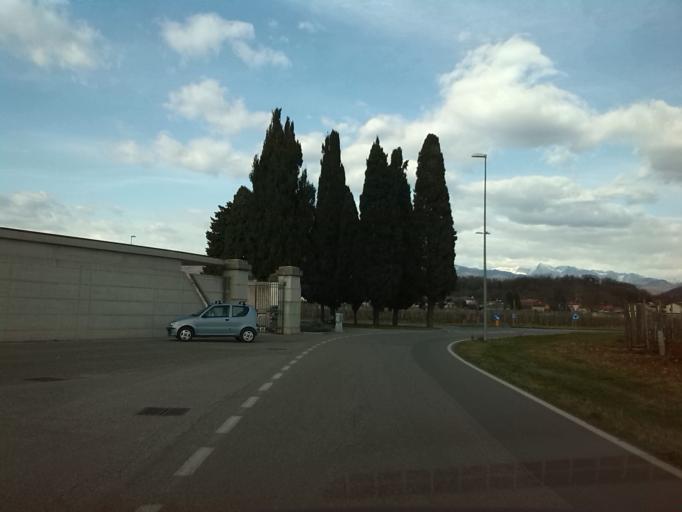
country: IT
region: Friuli Venezia Giulia
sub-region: Provincia di Udine
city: Cividale del Friuli
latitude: 46.0782
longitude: 13.4321
